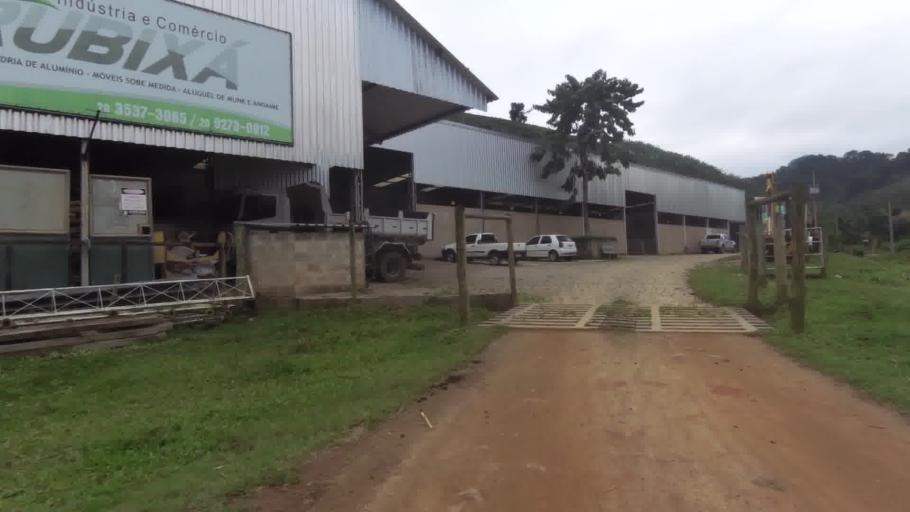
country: BR
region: Espirito Santo
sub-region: Iconha
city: Iconha
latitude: -20.7647
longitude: -40.8380
